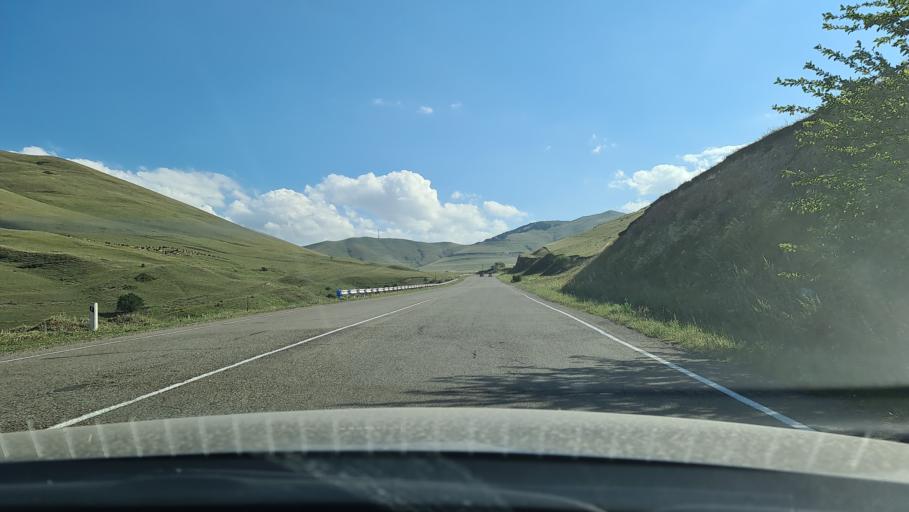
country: AM
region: Lorri
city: Saramech
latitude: 40.7586
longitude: 44.2105
